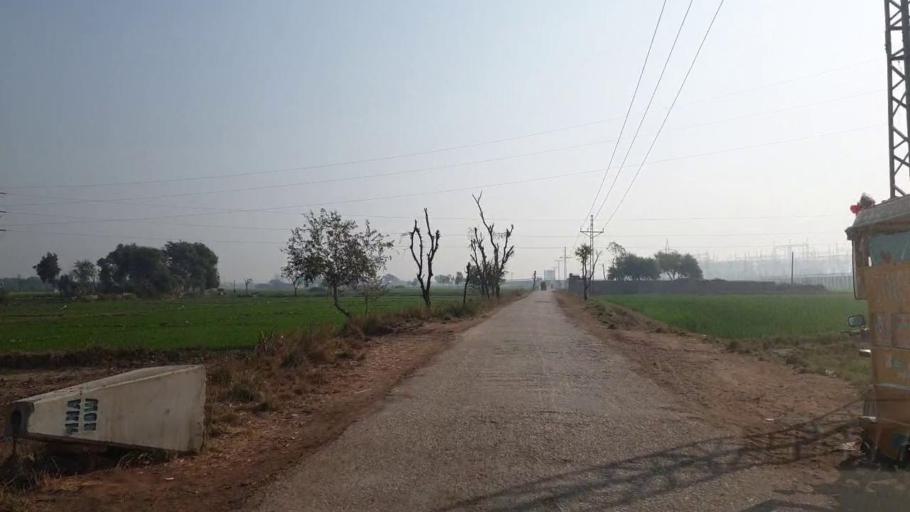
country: PK
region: Sindh
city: Bhit Shah
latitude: 25.7187
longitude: 68.5109
